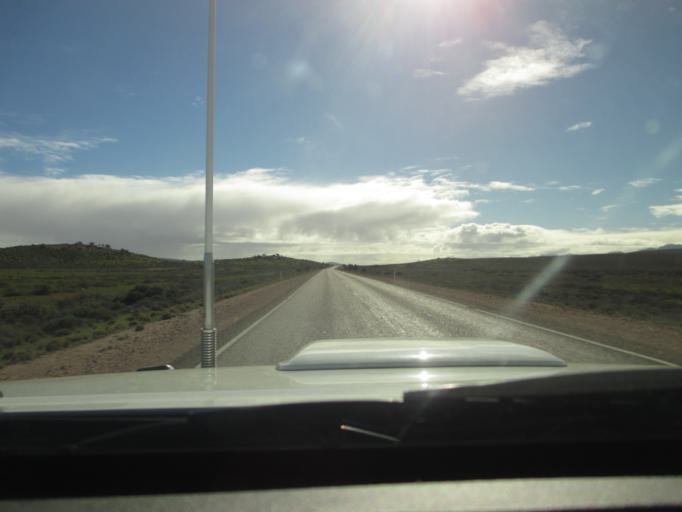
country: AU
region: South Australia
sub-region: Flinders Ranges
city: Quorn
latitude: -31.7475
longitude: 138.3370
